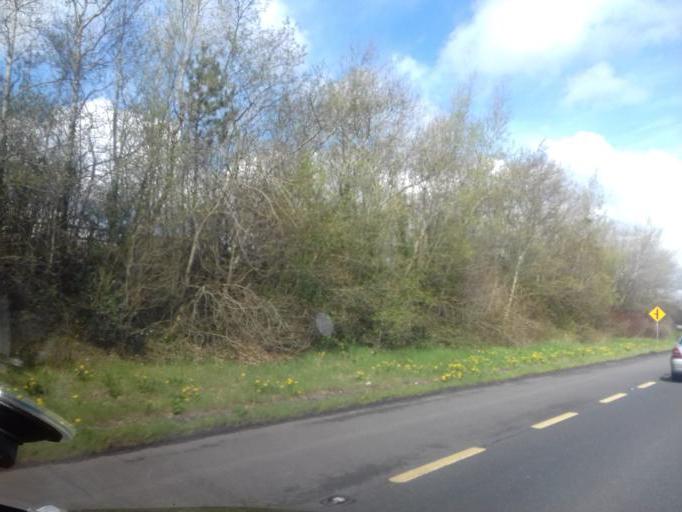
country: IE
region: Ulster
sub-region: An Cabhan
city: Belturbet
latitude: 54.1113
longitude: -7.4711
